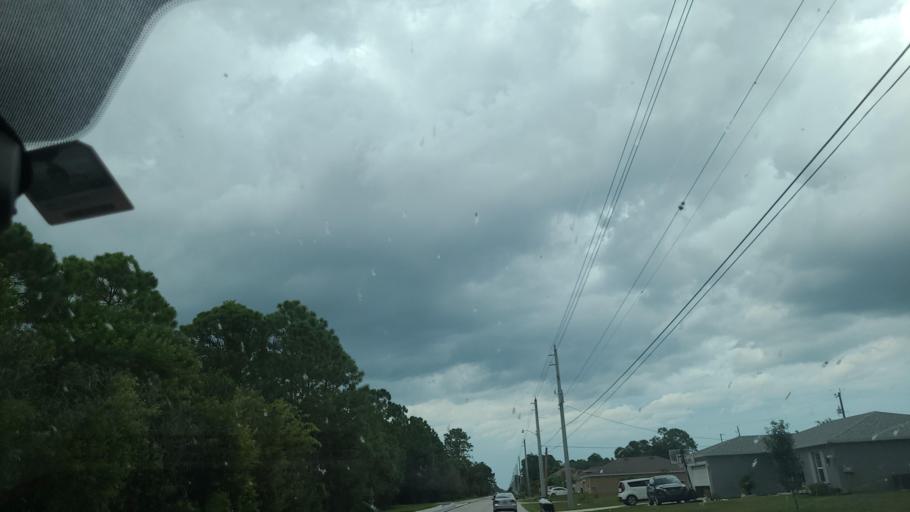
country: US
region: Florida
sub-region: Saint Lucie County
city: Port Saint Lucie
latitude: 27.2314
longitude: -80.3996
